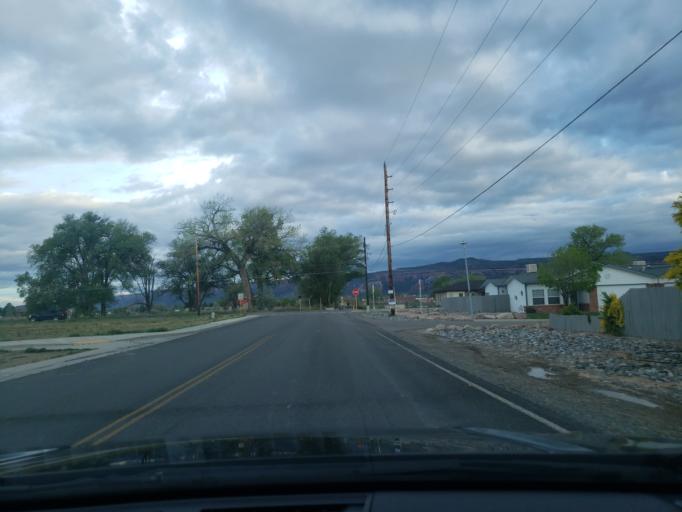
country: US
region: Colorado
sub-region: Mesa County
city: Fruita
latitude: 39.1651
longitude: -108.7105
